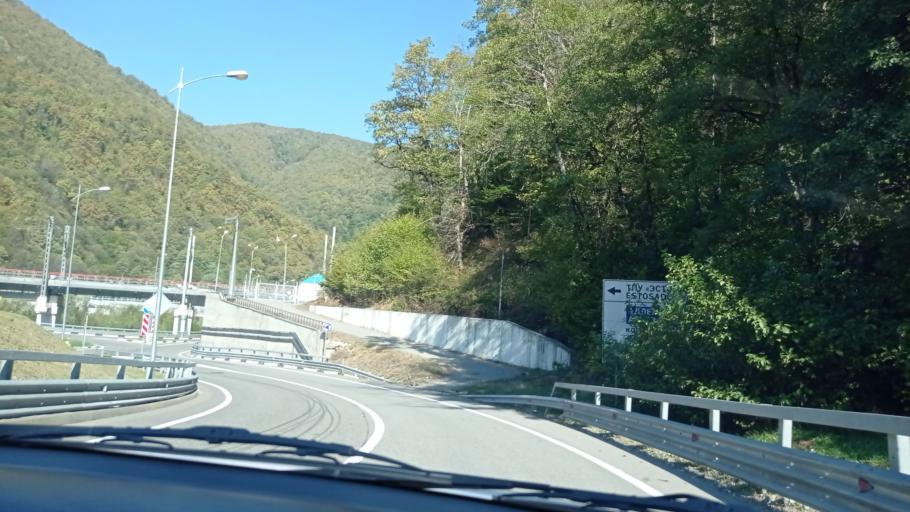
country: RU
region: Krasnodarskiy
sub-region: Sochi City
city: Krasnaya Polyana
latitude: 43.6832
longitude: 40.2456
